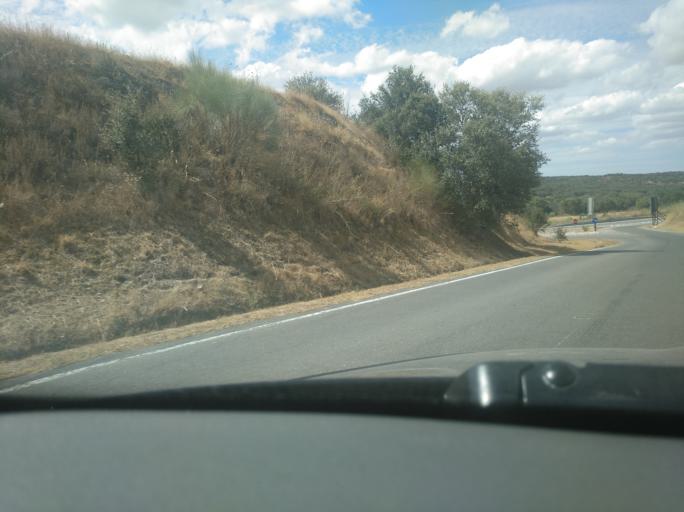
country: PT
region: Portalegre
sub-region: Arronches
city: Arronches
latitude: 39.0609
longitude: -7.4369
